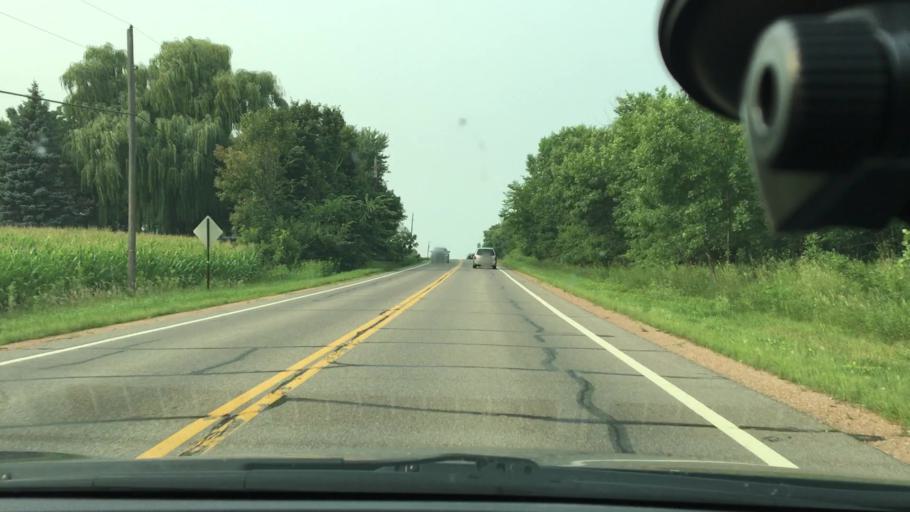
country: US
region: Minnesota
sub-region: Hennepin County
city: Osseo
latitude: 45.1445
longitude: -93.4620
